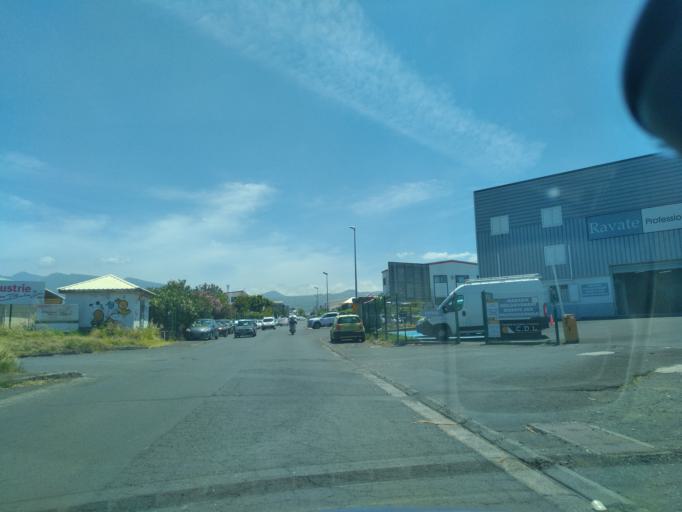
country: RE
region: Reunion
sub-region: Reunion
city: Saint-Pierre
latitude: -21.3193
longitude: 55.4515
